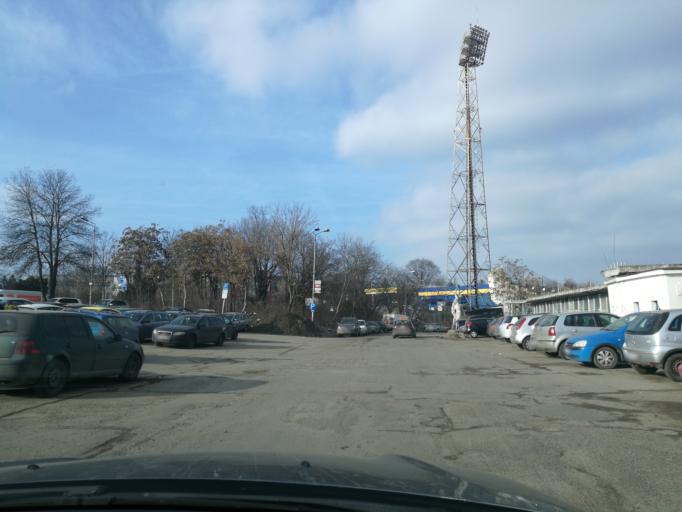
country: RO
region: Bacau
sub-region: Municipiul Bacau
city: Bacau
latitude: 46.5570
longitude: 26.9125
